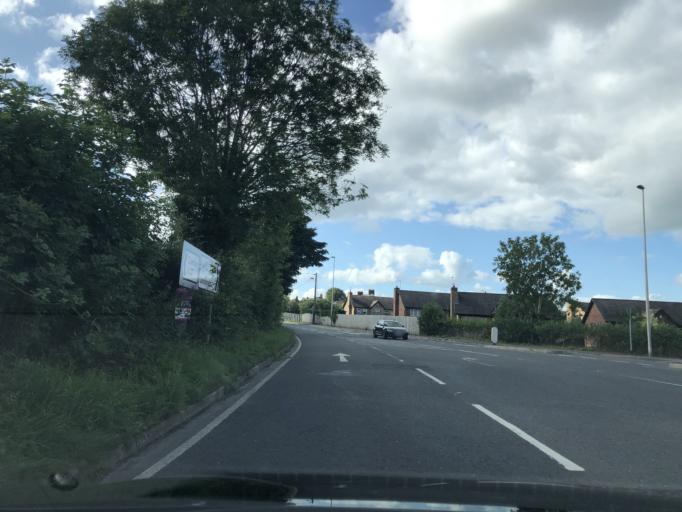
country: GB
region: Northern Ireland
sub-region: Castlereagh District
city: Dundonald
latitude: 54.5814
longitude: -5.7934
